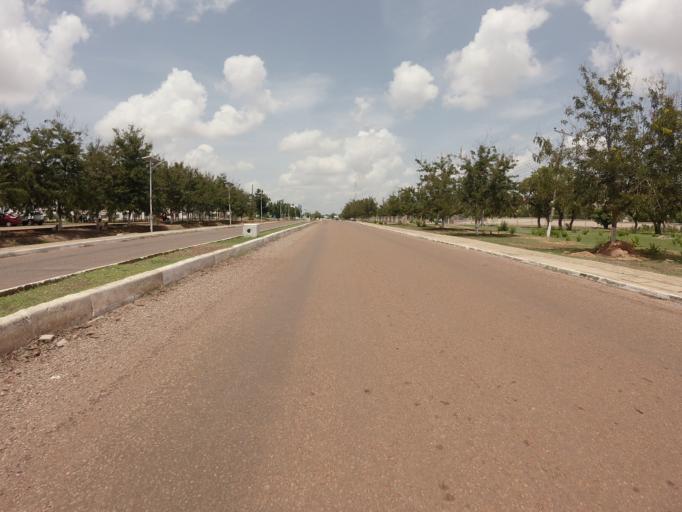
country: GH
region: Northern
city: Tamale
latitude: 9.3714
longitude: -0.8846
